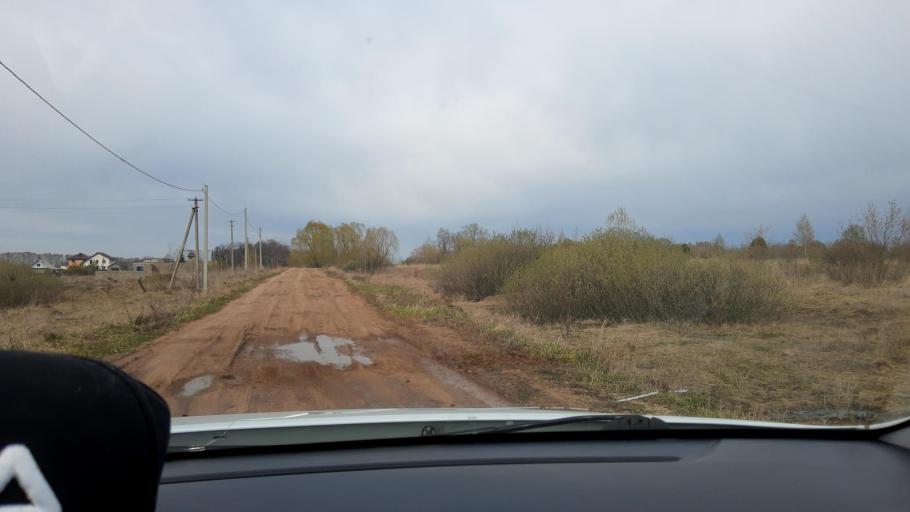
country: RU
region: Bashkortostan
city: Iglino
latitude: 54.8053
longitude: 56.4376
